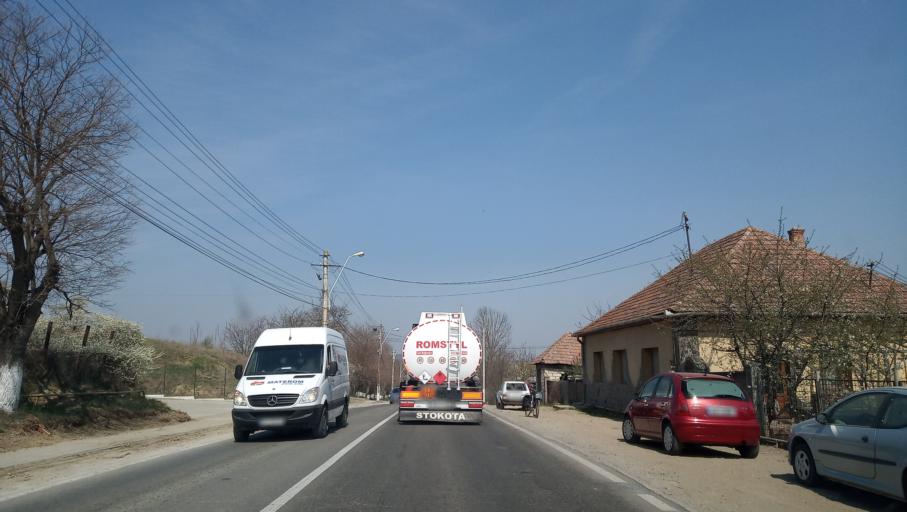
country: RO
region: Alba
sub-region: Oras Teius
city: Teius
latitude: 46.2121
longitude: 23.6772
